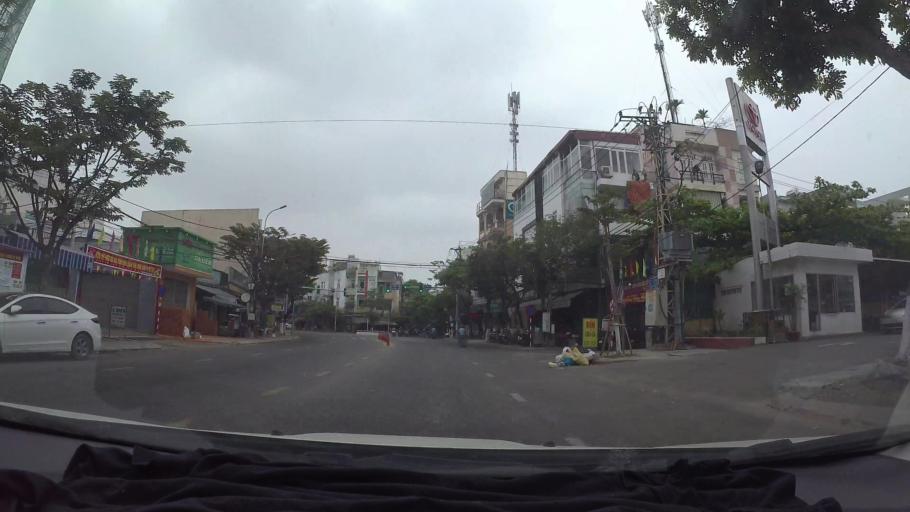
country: VN
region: Da Nang
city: Da Nang
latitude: 16.0544
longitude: 108.2118
